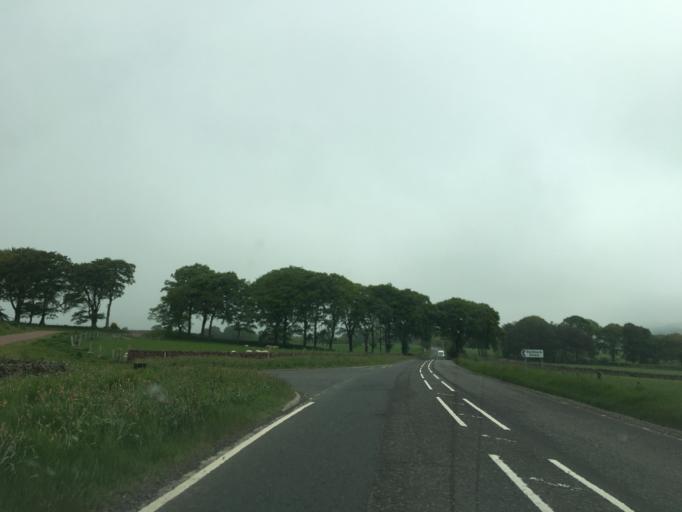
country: GB
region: Scotland
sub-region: The Scottish Borders
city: West Linton
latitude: 55.7108
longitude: -3.3508
